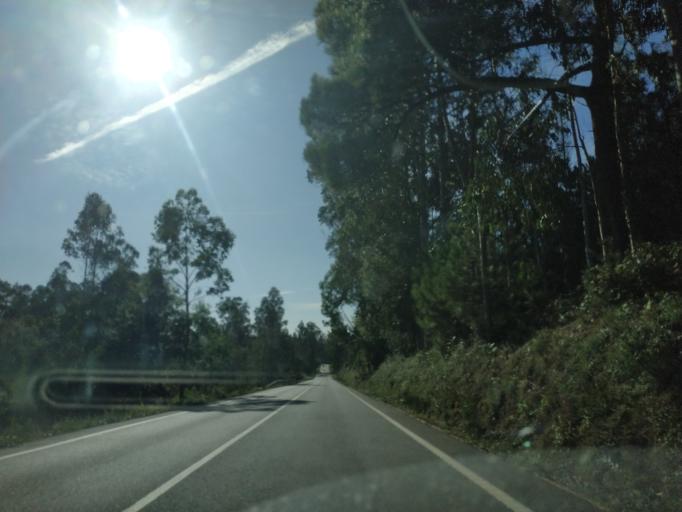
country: ES
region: Galicia
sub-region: Provincia da Coruna
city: Carballo
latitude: 43.1255
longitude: -8.6290
